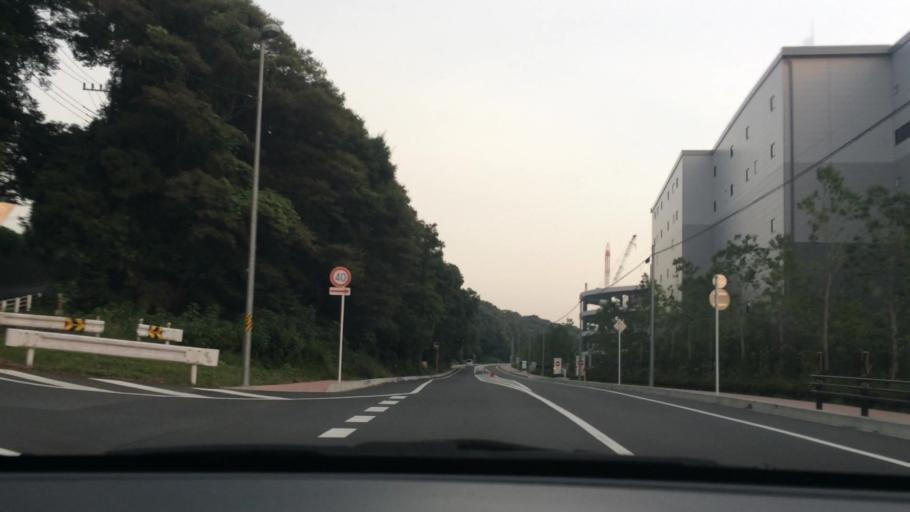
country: JP
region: Chiba
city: Nagareyama
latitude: 35.8886
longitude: 139.8987
